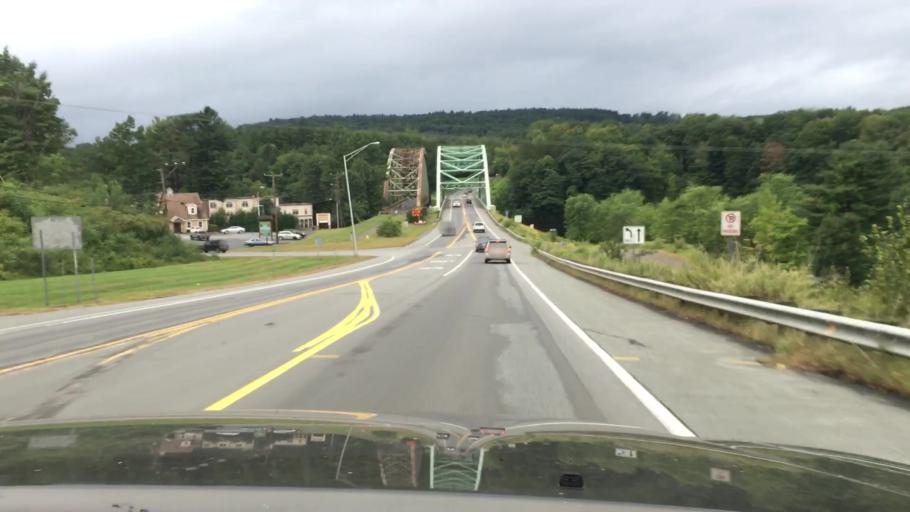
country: US
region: Vermont
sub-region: Windham County
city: Brattleboro
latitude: 42.8846
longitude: -72.5479
